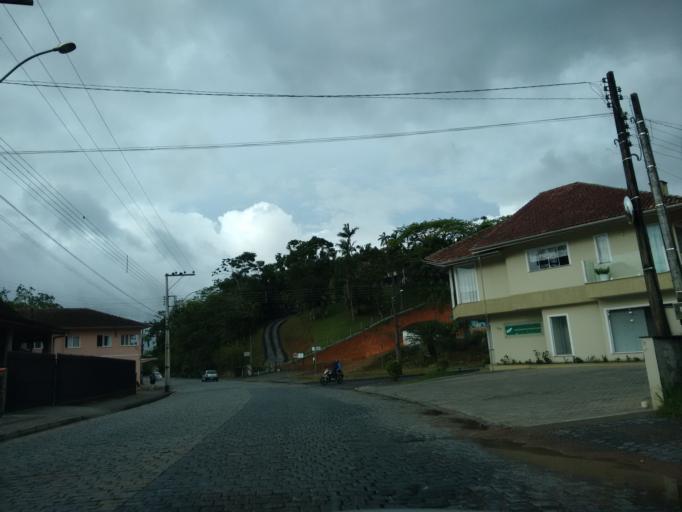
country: BR
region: Santa Catarina
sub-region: Pomerode
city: Pomerode
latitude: -26.7312
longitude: -49.1721
